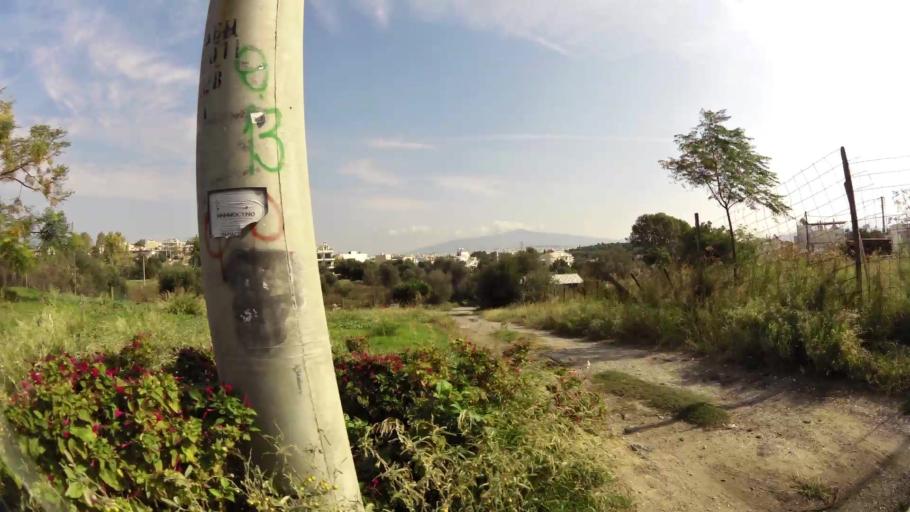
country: GR
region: Attica
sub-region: Nomarchia Athinas
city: Kamateron
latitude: 38.0471
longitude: 23.7082
